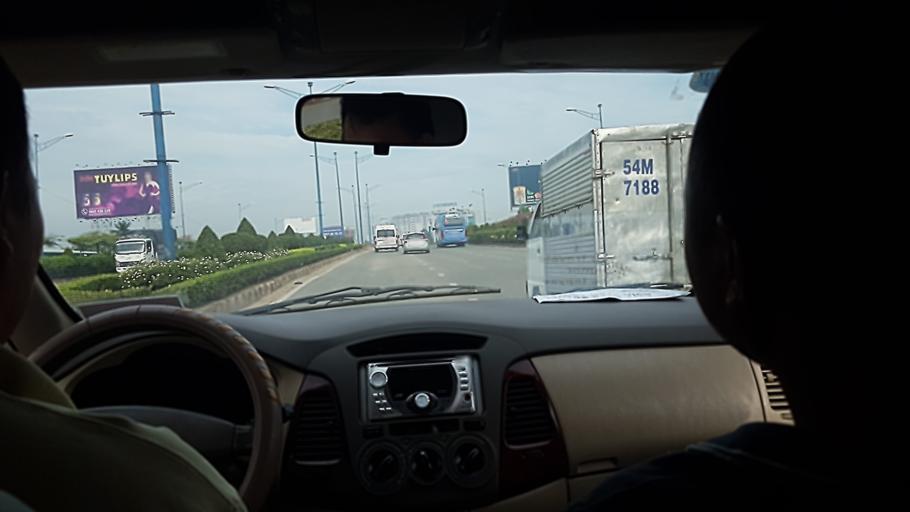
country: VN
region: Ho Chi Minh City
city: Ho Chi Minh City
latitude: 10.8239
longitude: 106.6289
